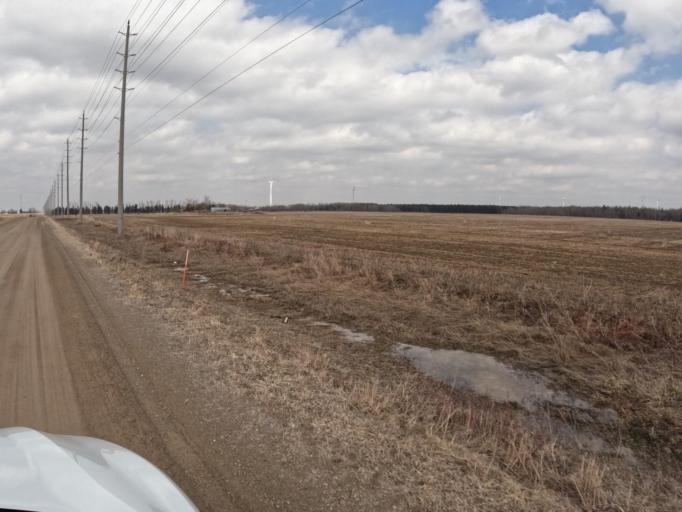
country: CA
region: Ontario
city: Shelburne
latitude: 44.0301
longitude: -80.3151
